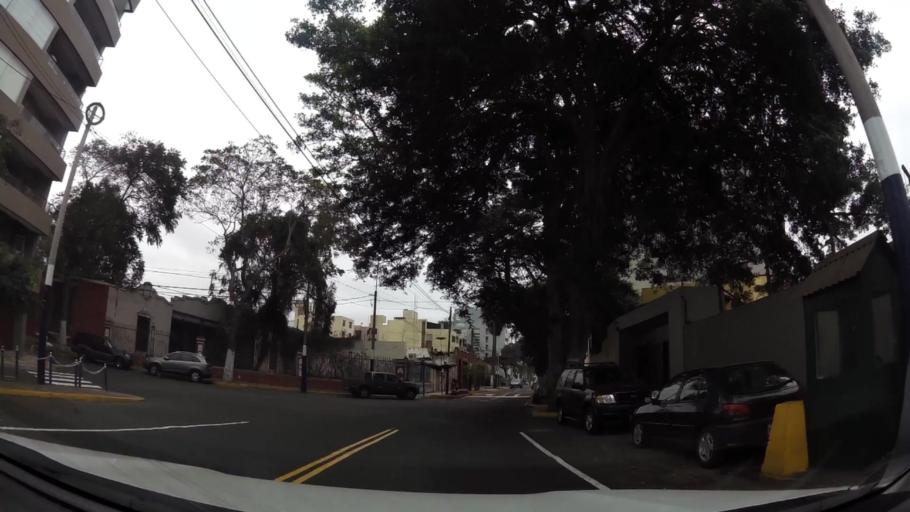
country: PE
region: Lima
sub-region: Lima
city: Surco
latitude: -12.1640
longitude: -77.0242
